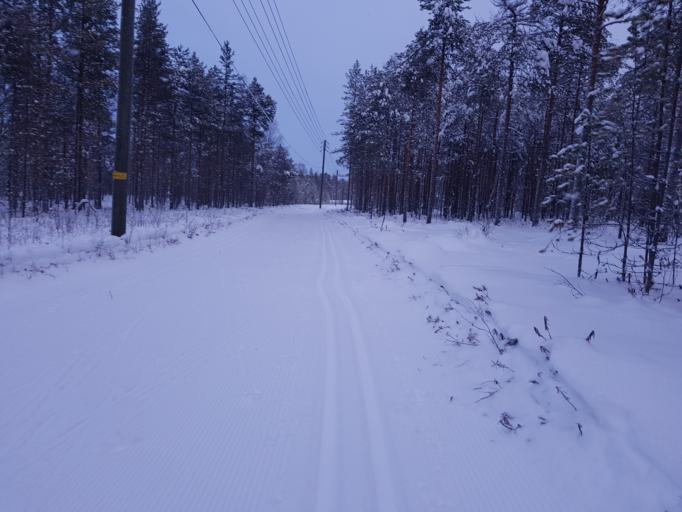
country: FI
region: Kainuu
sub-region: Kehys-Kainuu
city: Kuhmo
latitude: 64.1160
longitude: 29.5700
